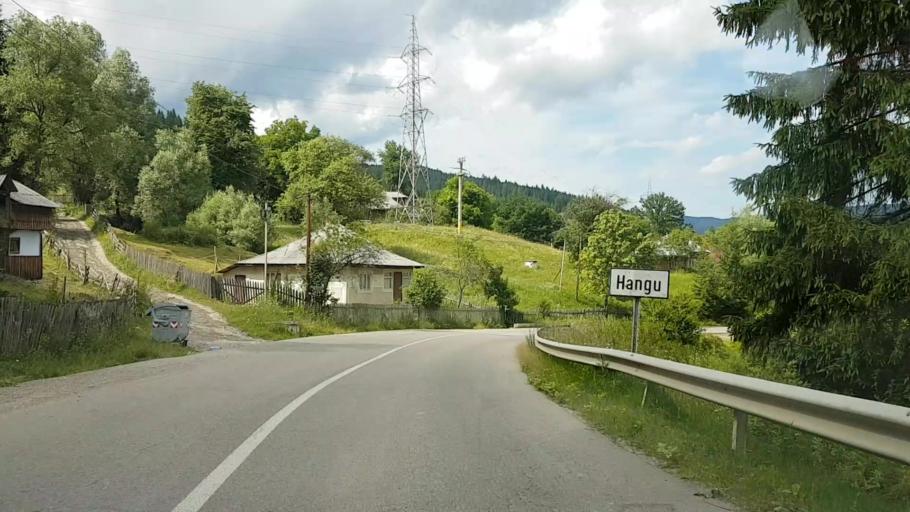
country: RO
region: Neamt
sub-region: Comuna Hangu
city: Hangu
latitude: 47.0569
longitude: 26.0308
